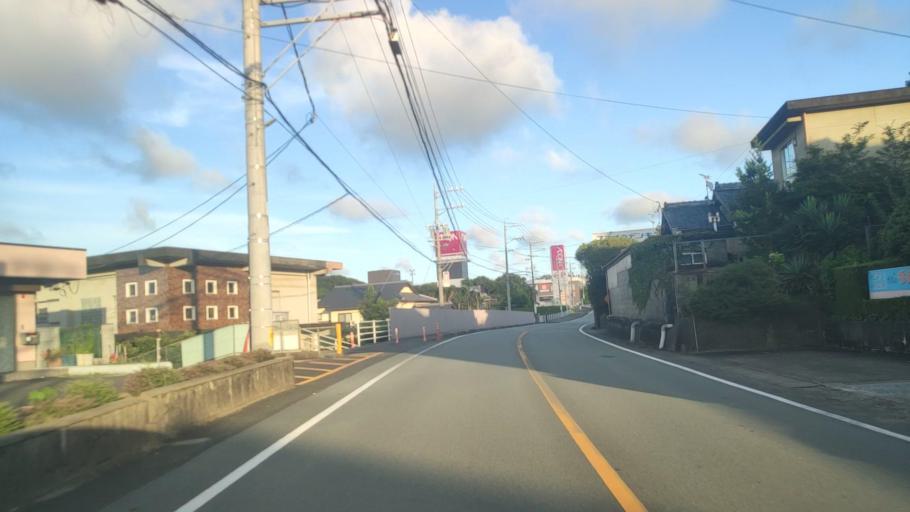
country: JP
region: Mie
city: Toba
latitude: 34.3250
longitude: 136.8266
